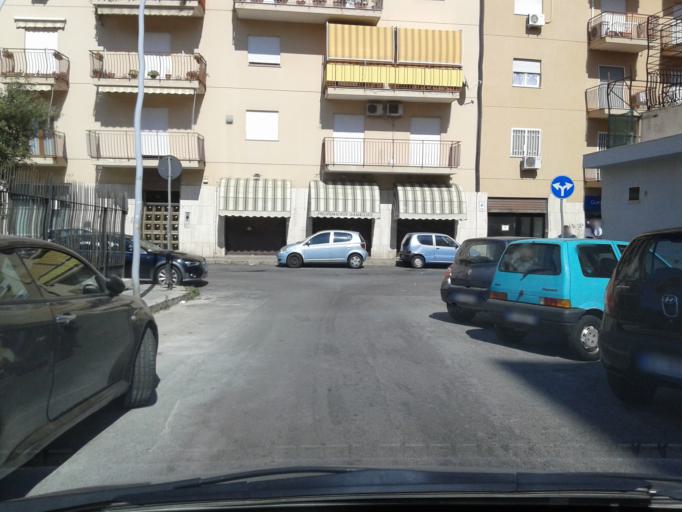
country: IT
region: Sicily
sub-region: Palermo
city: Palermo
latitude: 38.1064
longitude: 13.3371
